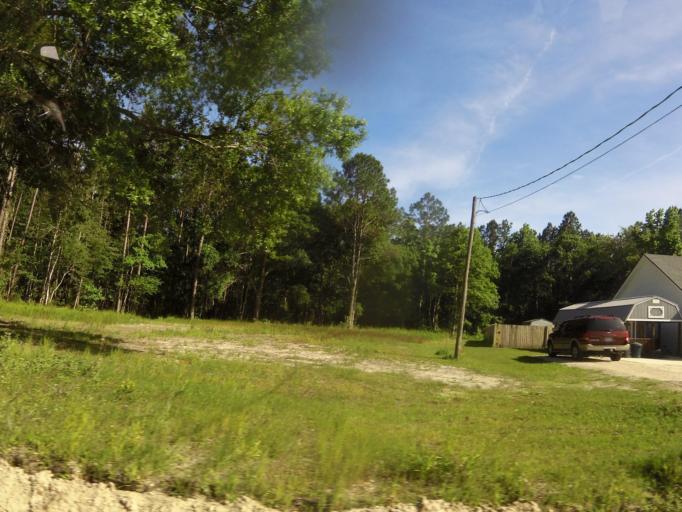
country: US
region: Florida
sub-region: Nassau County
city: Callahan
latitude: 30.5633
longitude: -81.7966
